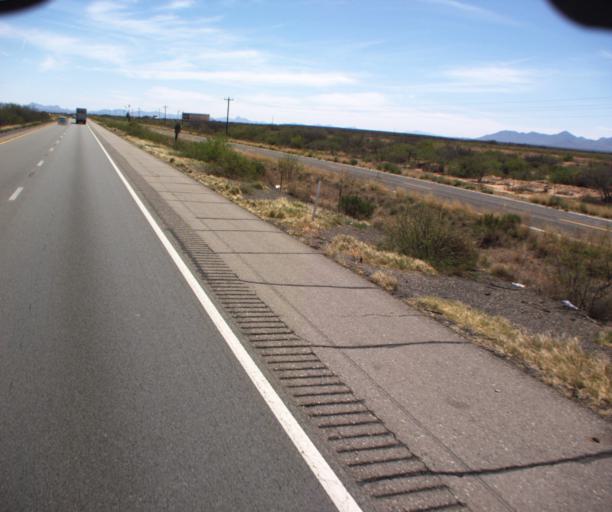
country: US
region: Arizona
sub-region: Cochise County
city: Willcox
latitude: 32.3144
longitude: -109.4296
